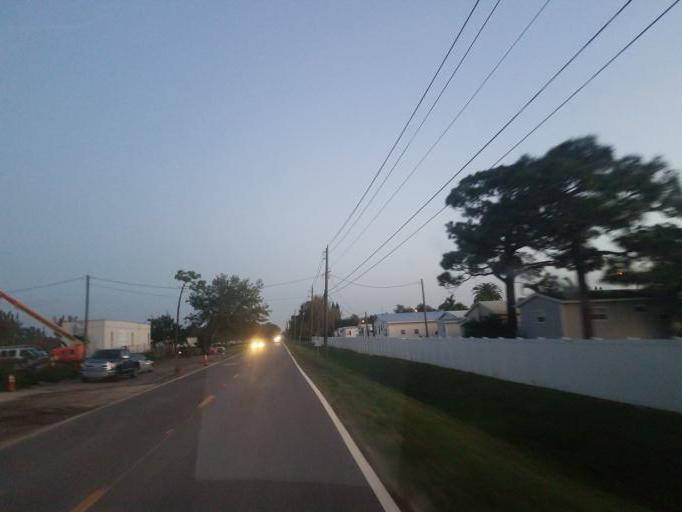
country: US
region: Florida
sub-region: Sarasota County
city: Bee Ridge
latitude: 27.2711
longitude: -82.4564
